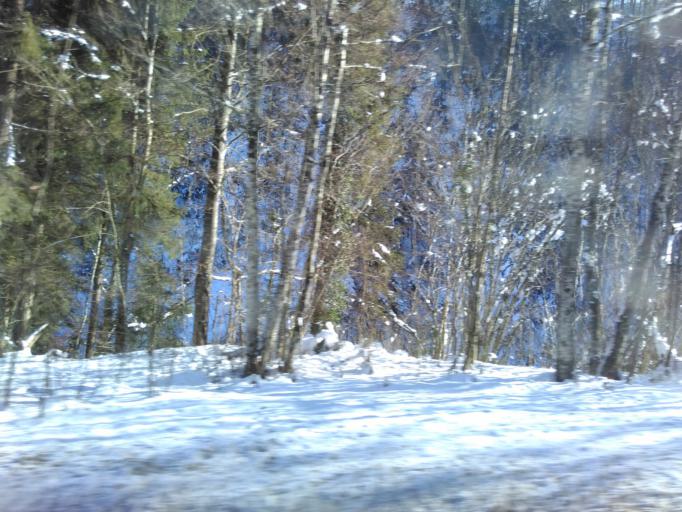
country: CH
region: Schwyz
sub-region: Bezirk March
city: Vorderthal
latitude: 47.1511
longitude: 8.8963
